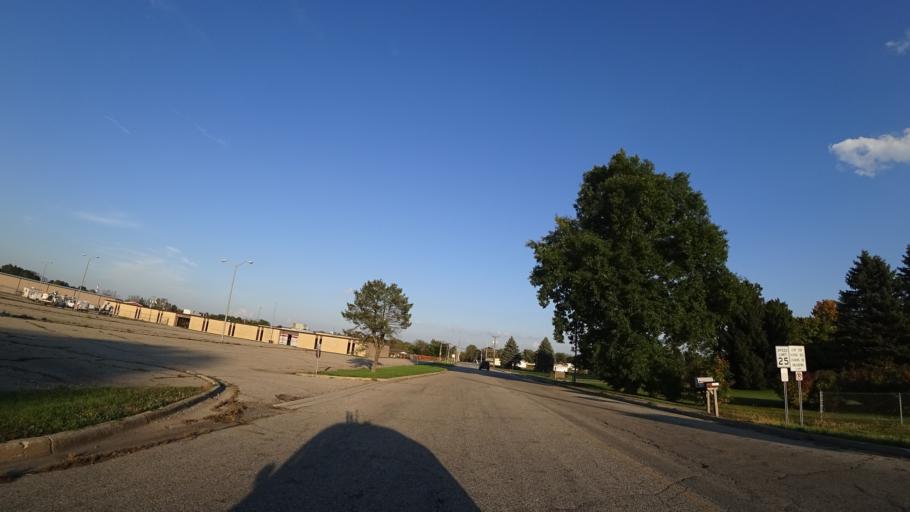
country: US
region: Michigan
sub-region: Saint Joseph County
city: Three Rivers
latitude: 41.9492
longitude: -85.6492
